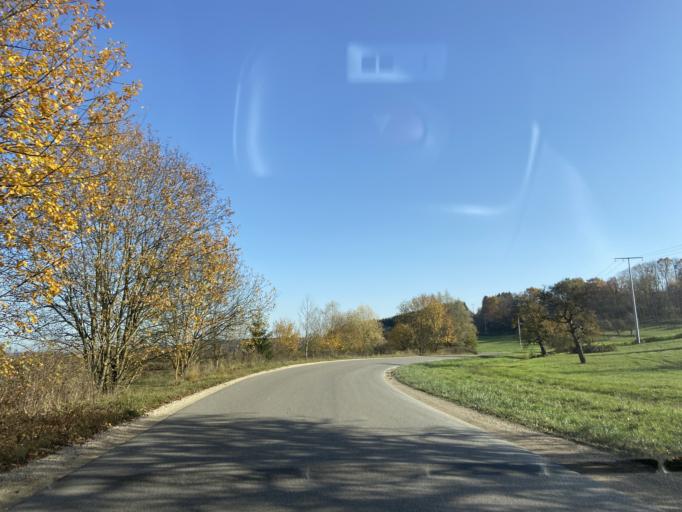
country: DE
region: Baden-Wuerttemberg
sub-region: Tuebingen Region
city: Krauchenwies
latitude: 48.0302
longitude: 9.2771
